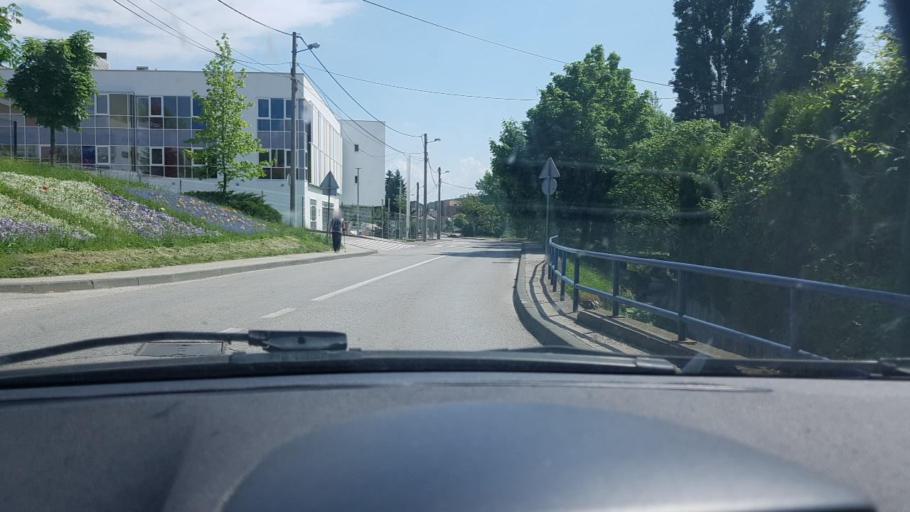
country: HR
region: Grad Zagreb
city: Kasina
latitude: 45.8757
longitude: 16.0154
